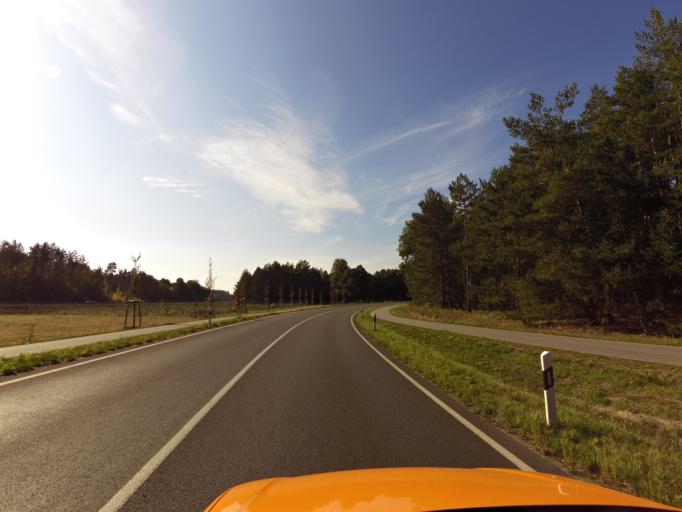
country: DE
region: Berlin
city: Wannsee
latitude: 52.3763
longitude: 13.1634
